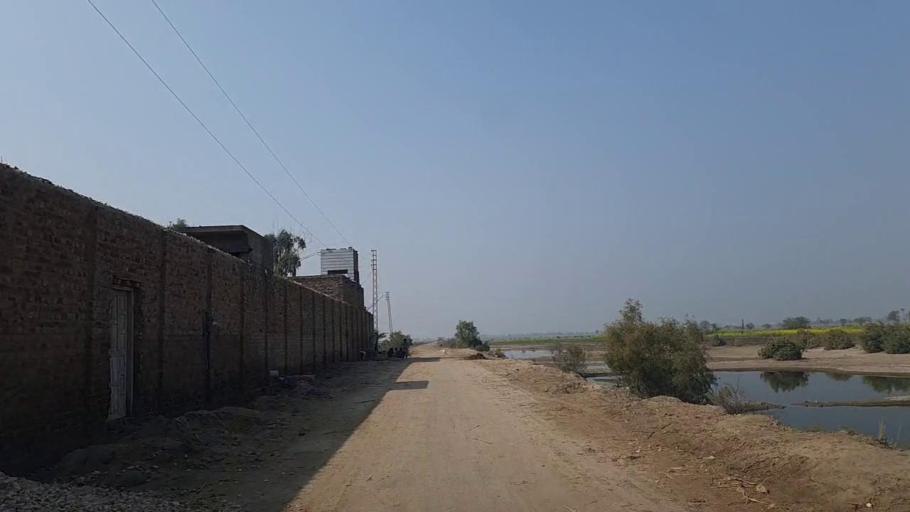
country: PK
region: Sindh
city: Nawabshah
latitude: 26.3602
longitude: 68.4213
